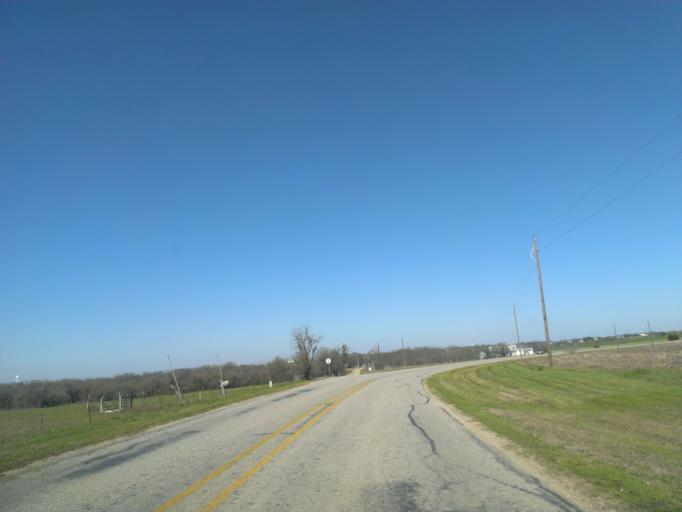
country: US
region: Texas
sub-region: Williamson County
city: Georgetown
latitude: 30.6827
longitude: -97.5893
